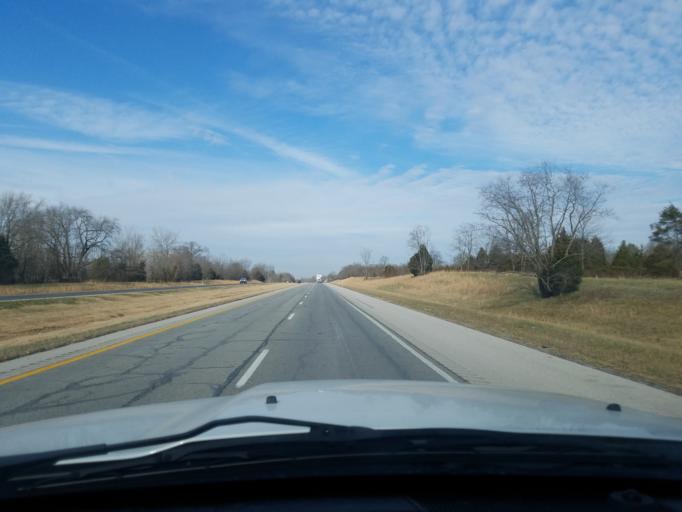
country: US
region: Indiana
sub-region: Monroe County
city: Bloomington
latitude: 39.0636
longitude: -86.5360
